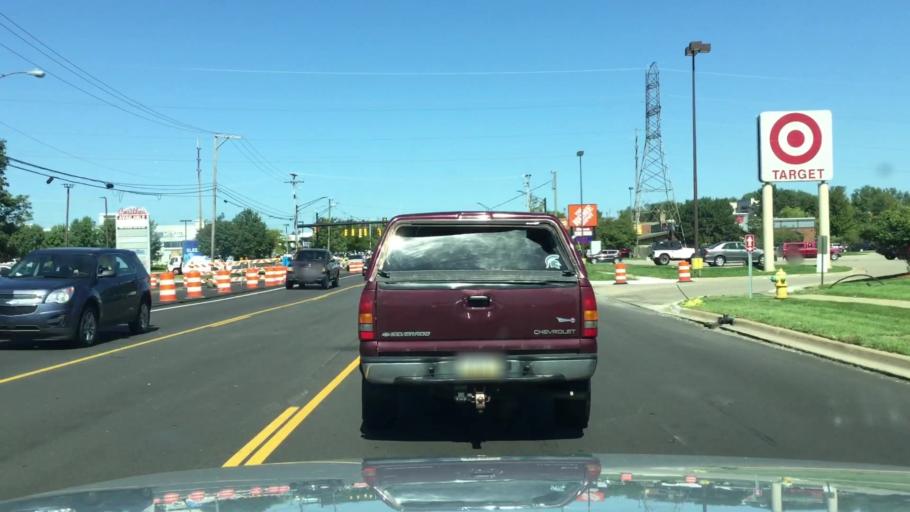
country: US
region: Michigan
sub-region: Kalamazoo County
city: Portage
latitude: 42.2181
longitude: -85.5894
